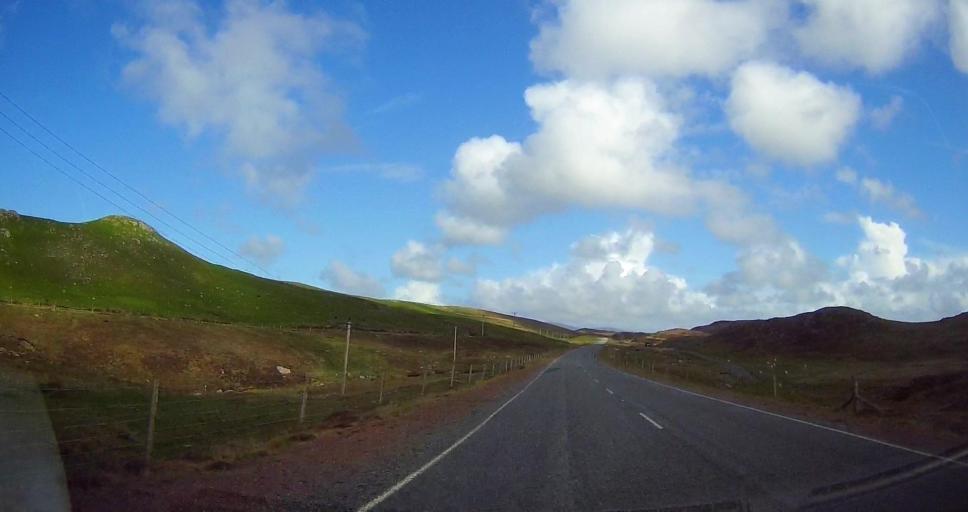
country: GB
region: Scotland
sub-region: Shetland Islands
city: Lerwick
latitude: 60.4241
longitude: -1.3955
